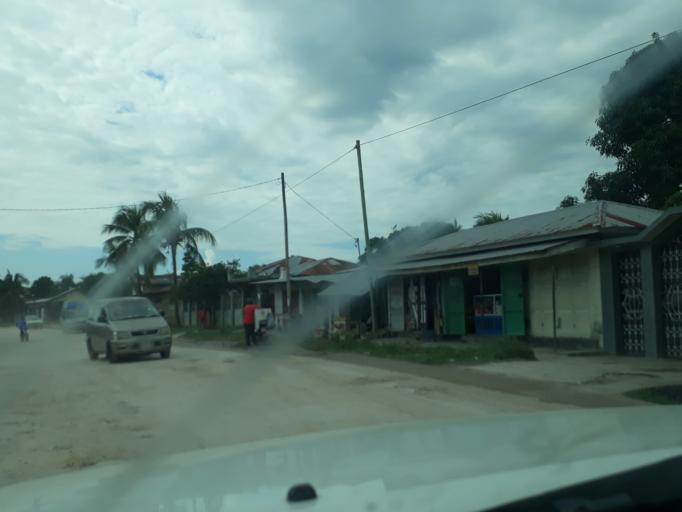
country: TZ
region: Zanzibar Central/South
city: Koani
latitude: -6.0838
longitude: 39.2228
